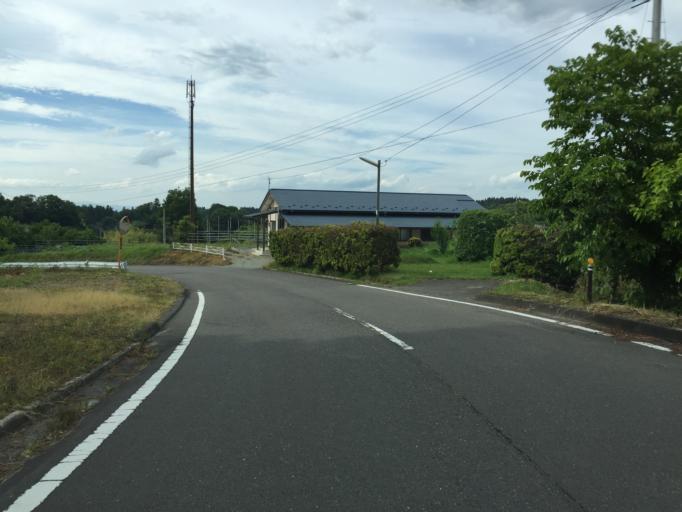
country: JP
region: Fukushima
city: Funehikimachi-funehiki
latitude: 37.5164
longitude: 140.5655
